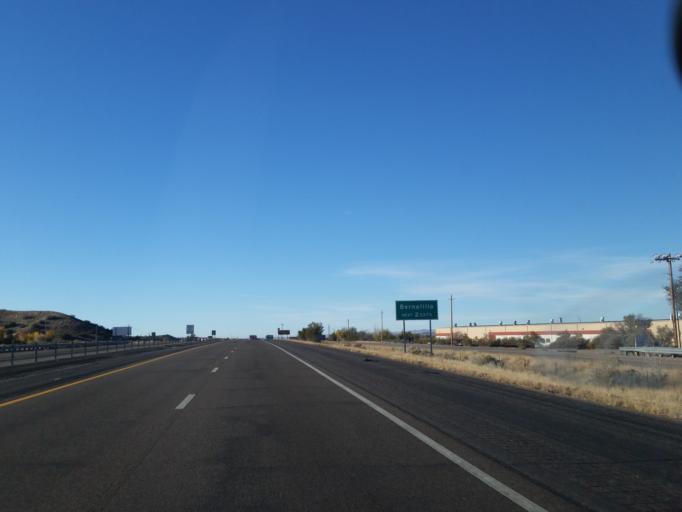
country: US
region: New Mexico
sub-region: Sandoval County
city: Bernalillo
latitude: 35.3305
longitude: -106.5247
